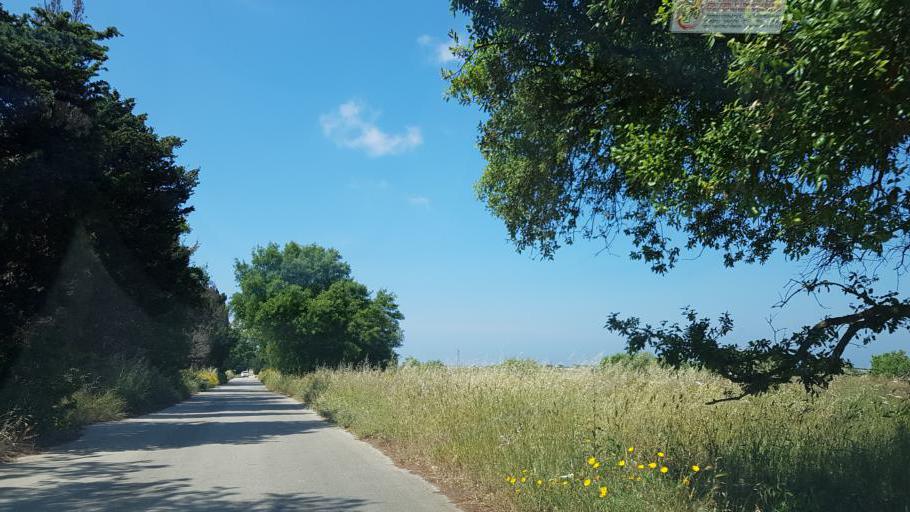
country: IT
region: Apulia
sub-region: Provincia di Brindisi
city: Brindisi
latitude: 40.6503
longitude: 17.8548
